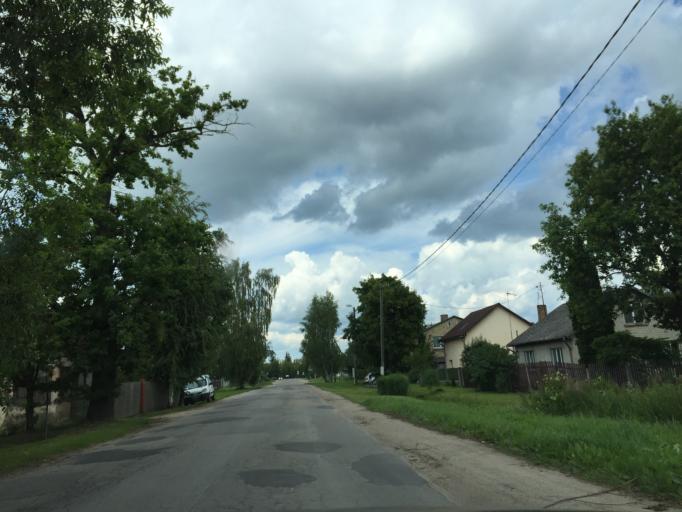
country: LV
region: Jelgava
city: Jelgava
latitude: 56.6276
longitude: 23.7053
